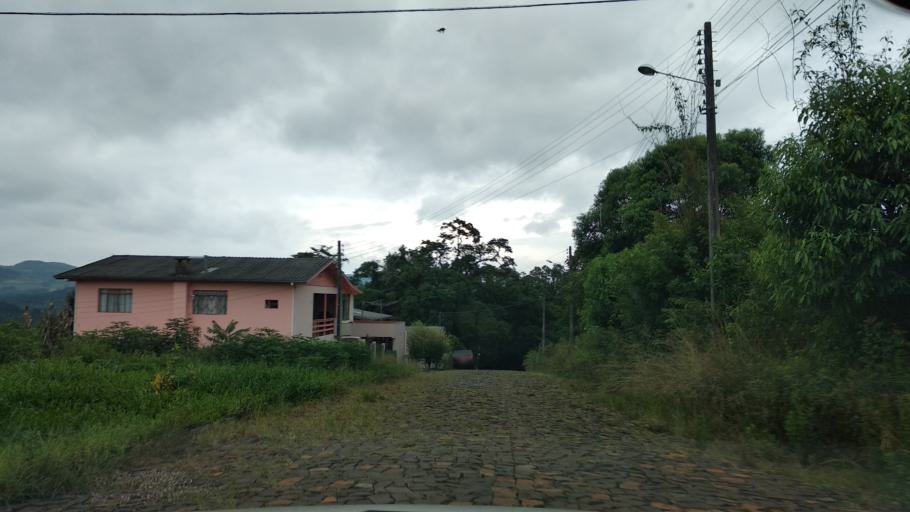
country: BR
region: Santa Catarina
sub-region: Videira
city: Videira
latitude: -26.9856
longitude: -51.1705
